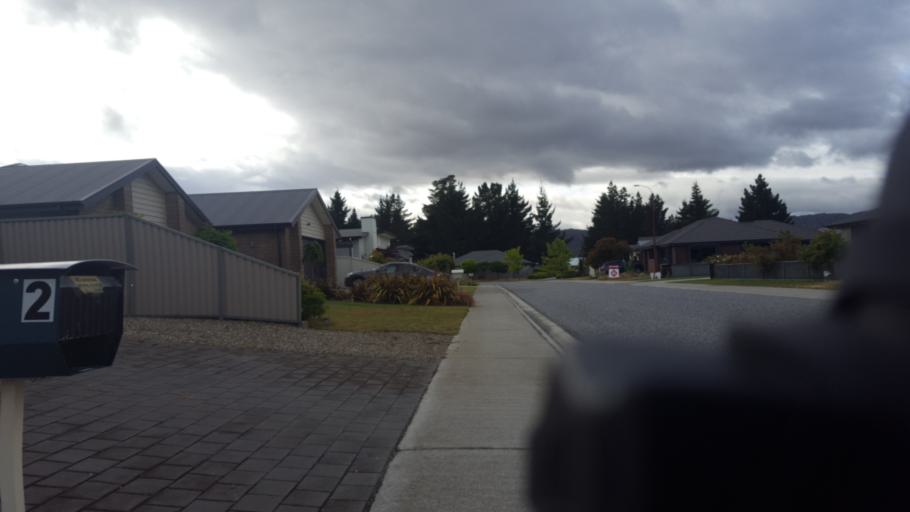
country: NZ
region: Otago
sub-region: Queenstown-Lakes District
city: Wanaka
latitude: -45.2402
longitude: 169.3797
